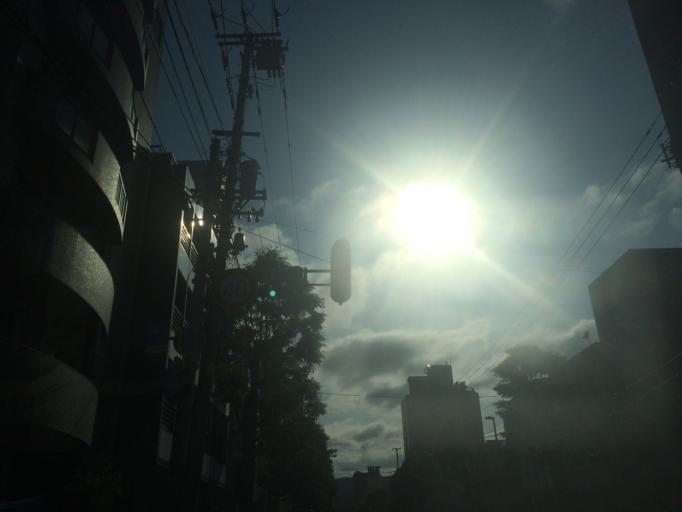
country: JP
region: Hokkaido
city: Sapporo
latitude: 43.0379
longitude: 141.3511
